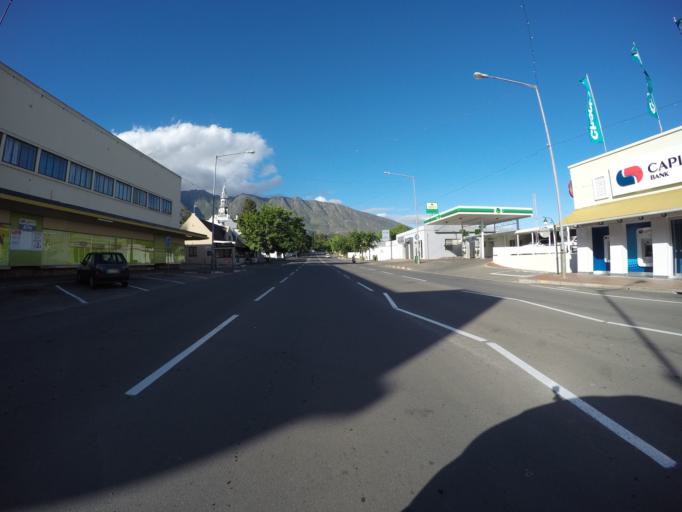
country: ZA
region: Western Cape
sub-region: Overberg District Municipality
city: Swellendam
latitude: -34.0188
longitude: 20.4457
